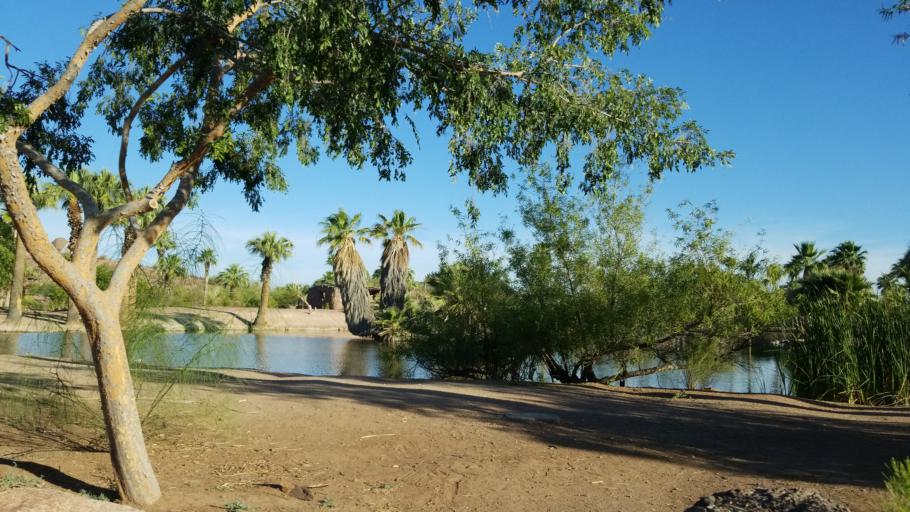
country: US
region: Arizona
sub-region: Maricopa County
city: Tempe Junction
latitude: 33.4543
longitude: -111.9477
